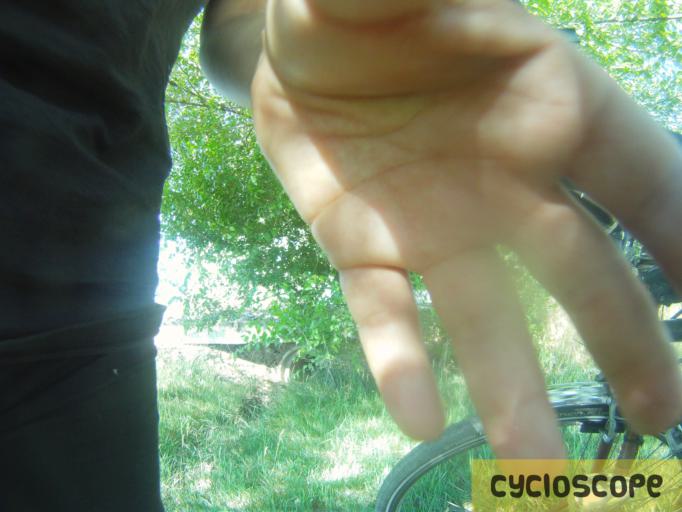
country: KZ
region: Almaty Oblysy
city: Zharkent
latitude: 44.2241
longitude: 80.2269
